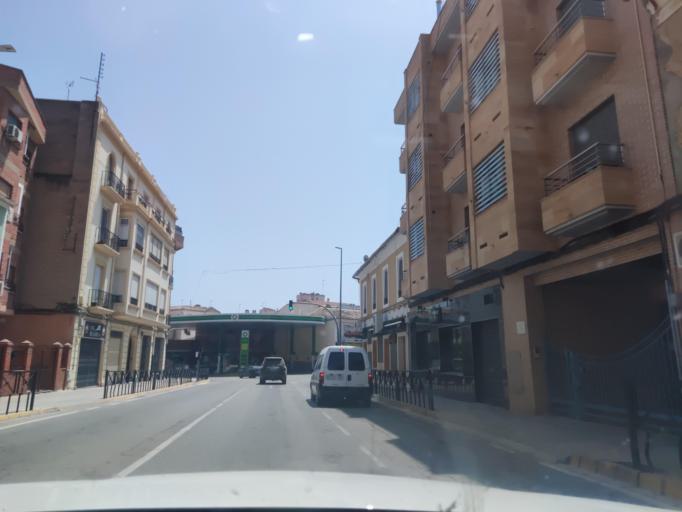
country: ES
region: Castille-La Mancha
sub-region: Provincia de Albacete
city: Hellin
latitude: 38.5120
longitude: -1.6972
